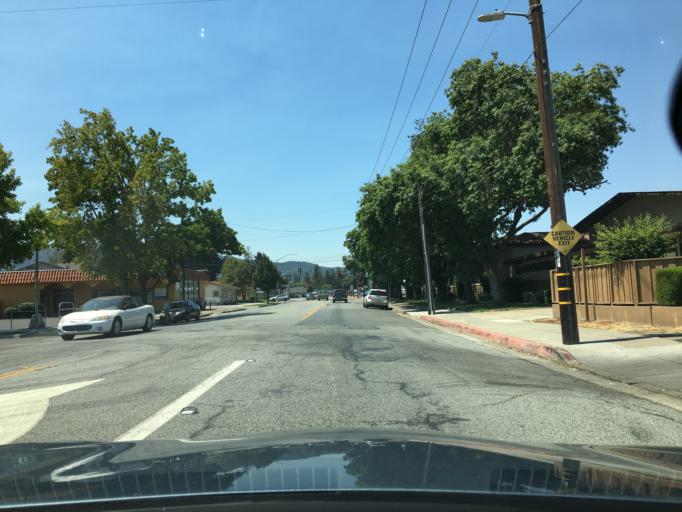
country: US
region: California
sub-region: Santa Clara County
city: Gilroy
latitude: 37.0144
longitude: -121.5731
